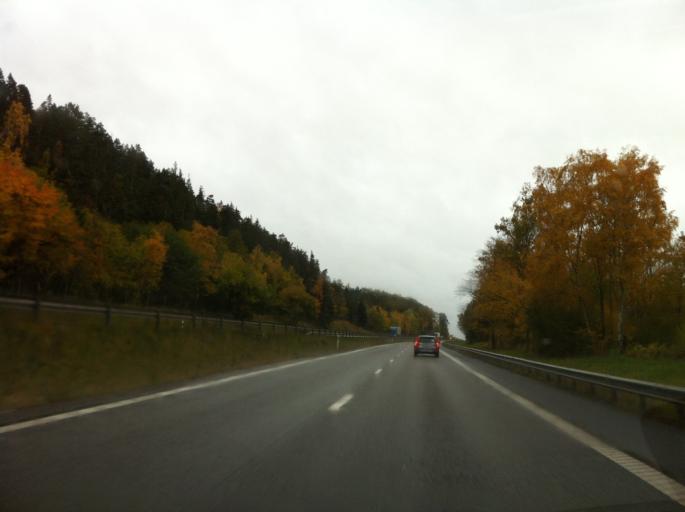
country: SE
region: Joenkoeping
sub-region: Jonkopings Kommun
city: Kaxholmen
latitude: 57.8864
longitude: 14.2835
